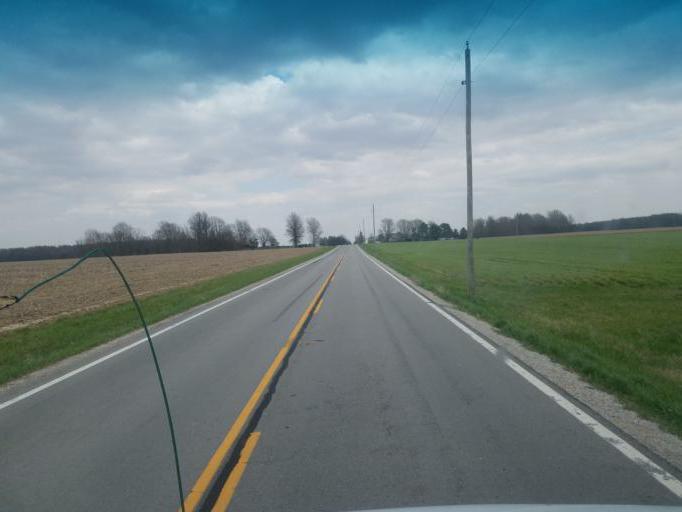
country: US
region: Ohio
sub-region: Crawford County
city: Bucyrus
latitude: 40.9504
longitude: -83.0584
